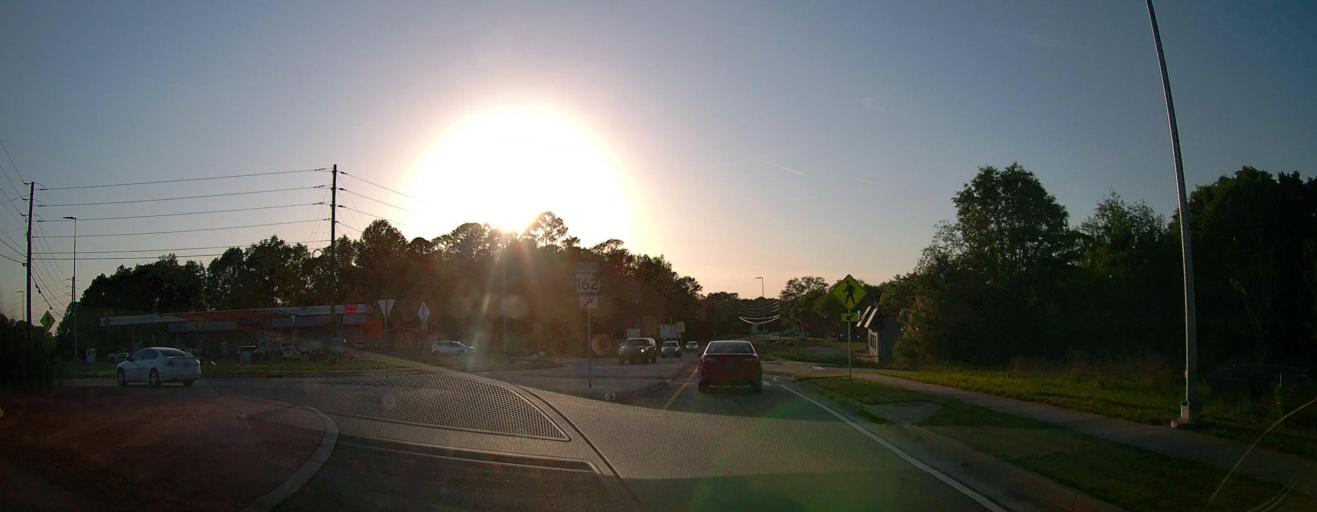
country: US
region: Georgia
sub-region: Newton County
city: Porterdale
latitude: 33.5572
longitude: -83.9218
